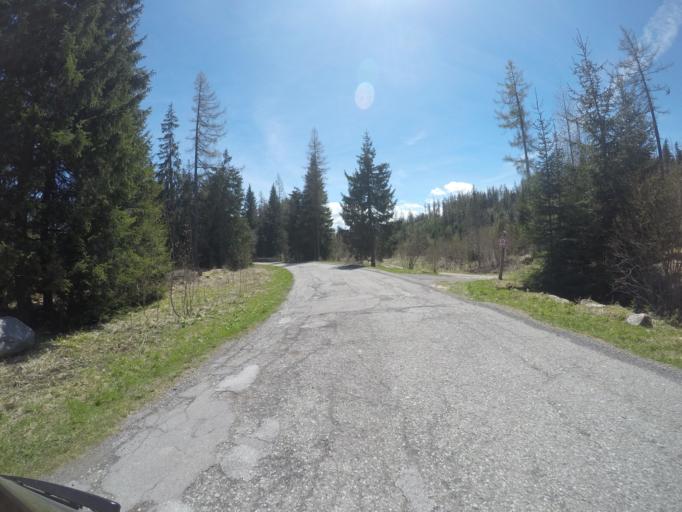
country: SK
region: Presovsky
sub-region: Okres Poprad
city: Strba
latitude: 49.1201
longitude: 20.0753
